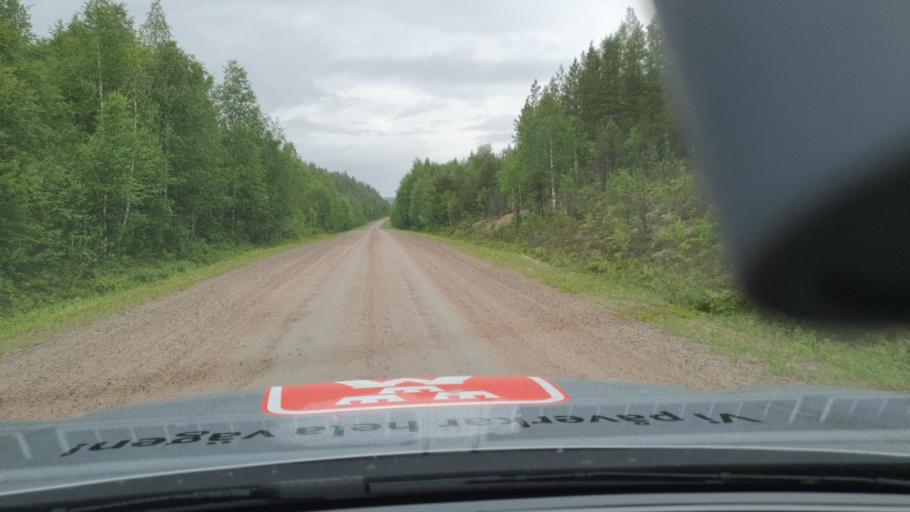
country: SE
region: Norrbotten
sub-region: Overkalix Kommun
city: OEverkalix
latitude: 66.5878
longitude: 22.7462
